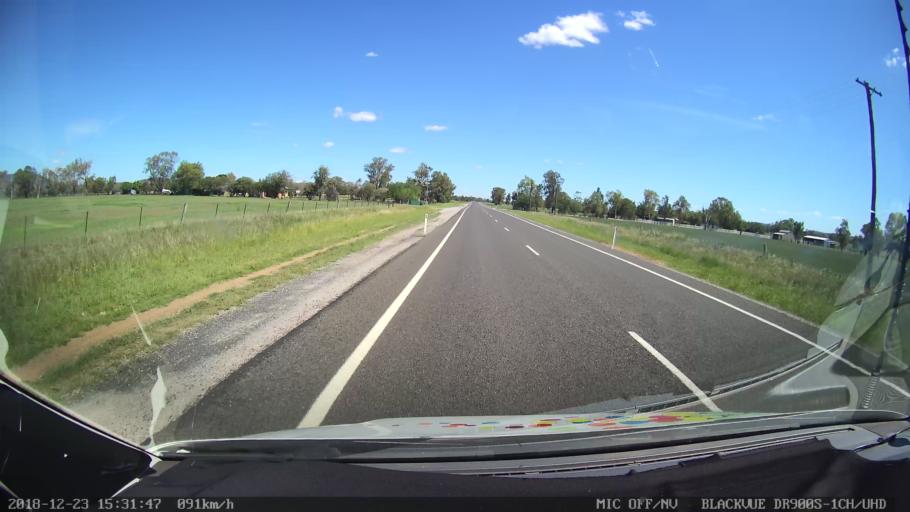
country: AU
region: New South Wales
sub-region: Tamworth Municipality
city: East Tamworth
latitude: -30.9766
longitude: 150.8686
